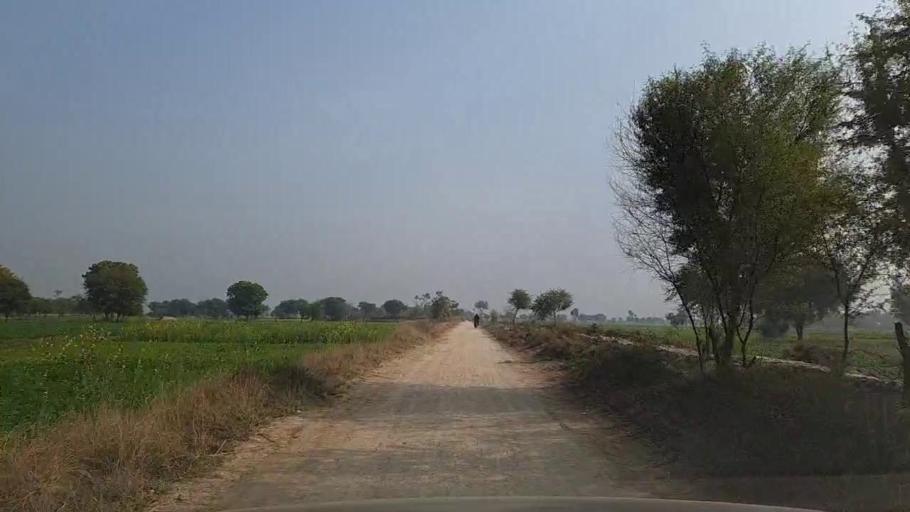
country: PK
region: Sindh
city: Nawabshah
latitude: 26.2897
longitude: 68.4428
